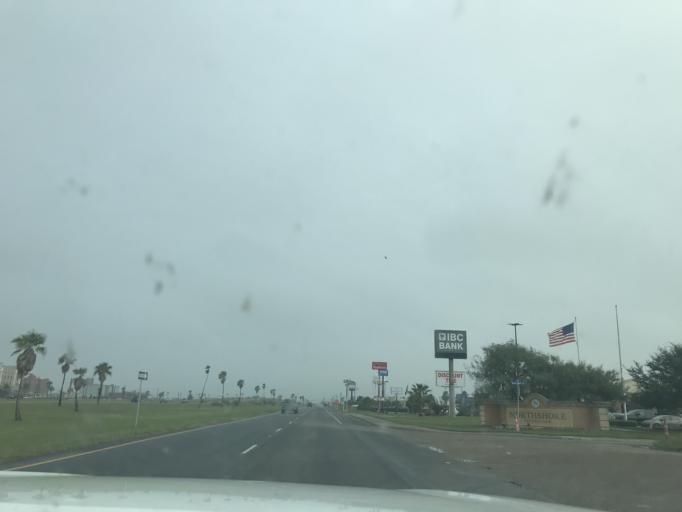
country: US
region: Texas
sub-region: San Patricio County
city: Portland
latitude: 27.8911
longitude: -97.3109
